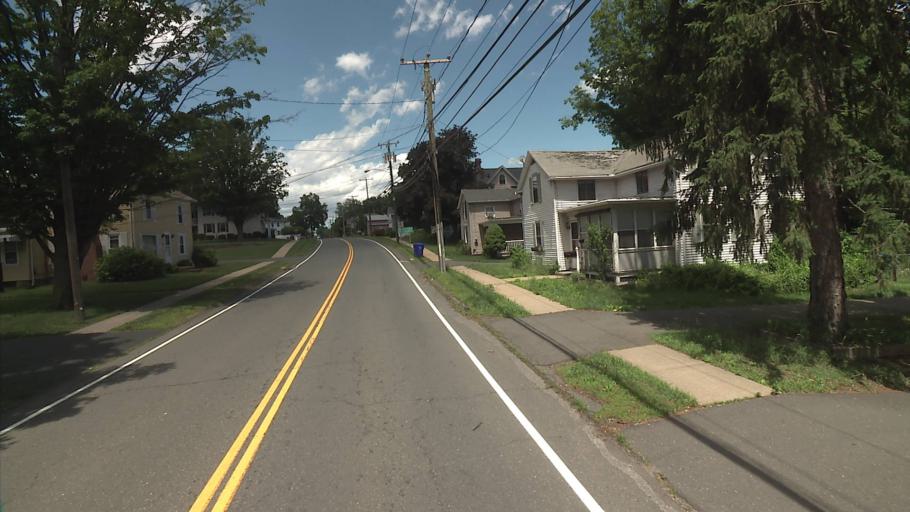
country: US
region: Connecticut
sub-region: Hartford County
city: Hazardville
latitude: 41.9872
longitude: -72.5393
